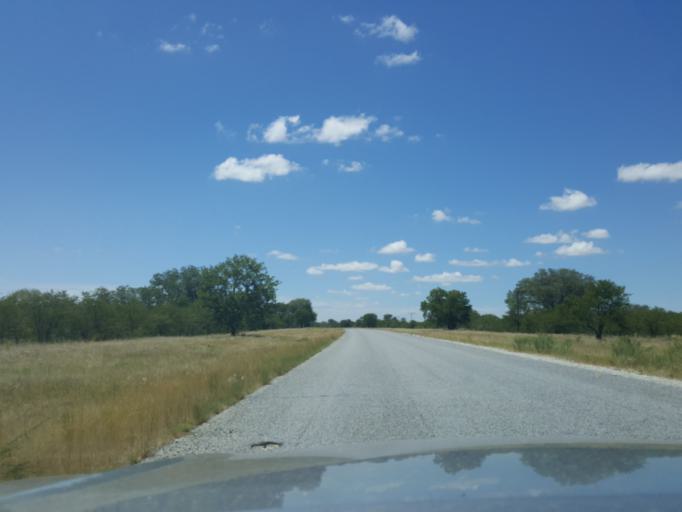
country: BW
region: Central
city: Nata
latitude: -20.1496
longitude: 25.7362
